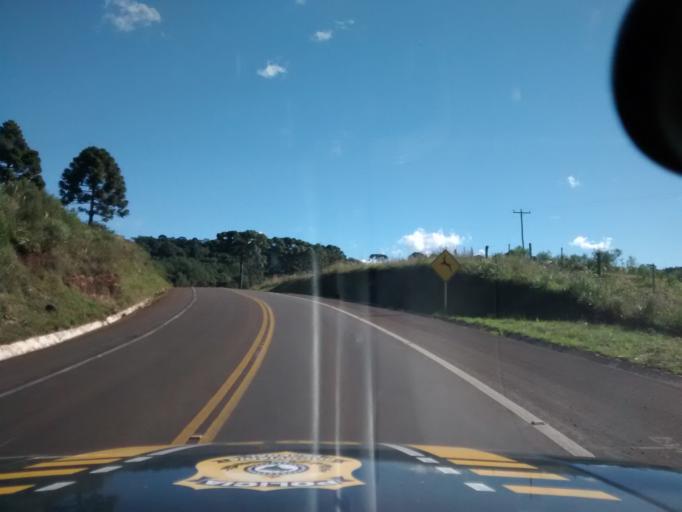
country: BR
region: Rio Grande do Sul
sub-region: Vacaria
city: Vacaria
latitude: -28.3316
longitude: -51.1657
